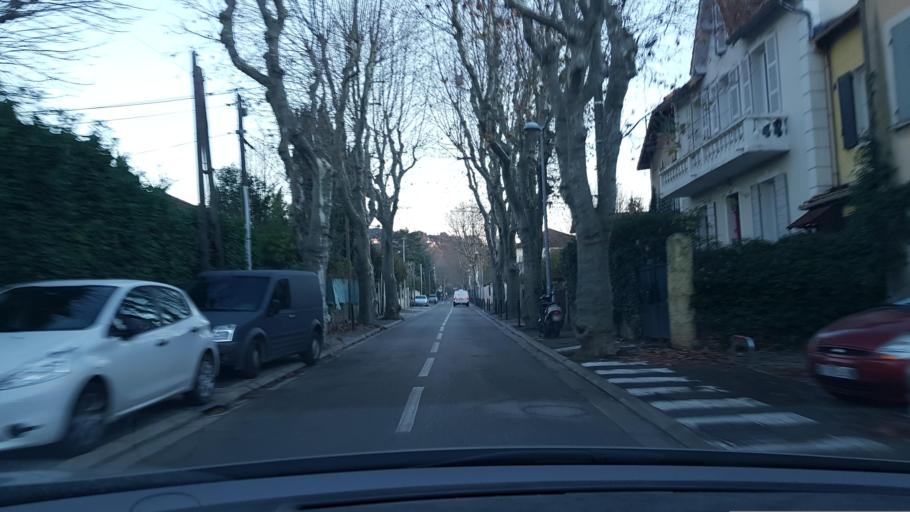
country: FR
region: Provence-Alpes-Cote d'Azur
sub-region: Departement des Bouches-du-Rhone
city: Bouc-Bel-Air
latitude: 43.4837
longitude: 5.4201
